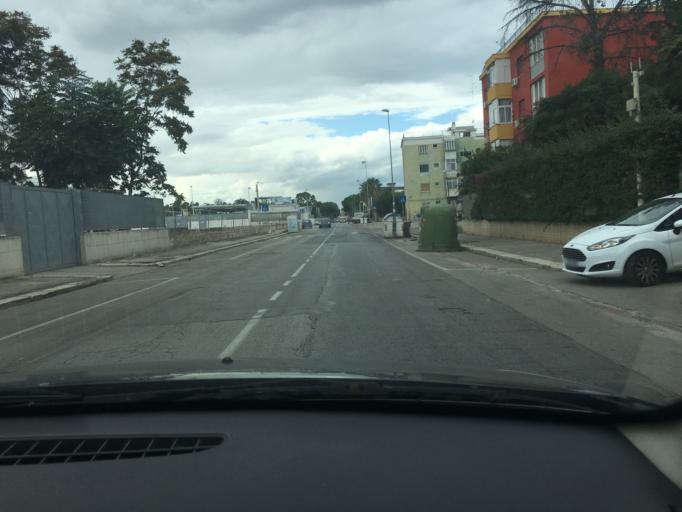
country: IT
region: Apulia
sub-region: Provincia di Bari
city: Bari
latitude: 41.1309
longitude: 16.8371
